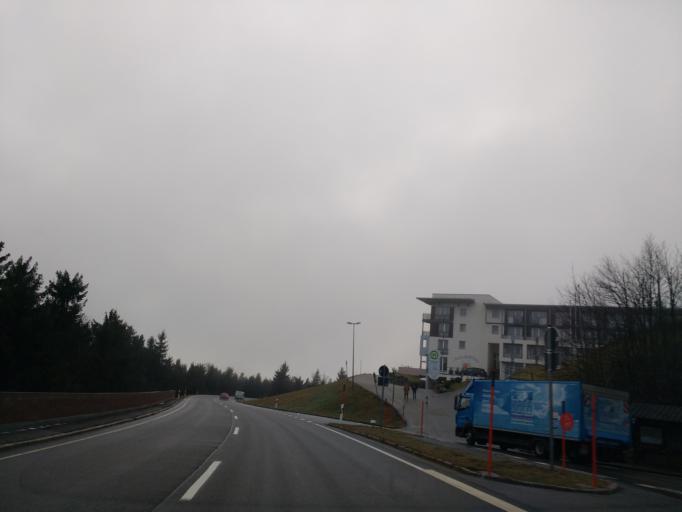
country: DE
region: Baden-Wuerttemberg
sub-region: Freiburg Region
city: Seebach
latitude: 48.5329
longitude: 8.2181
